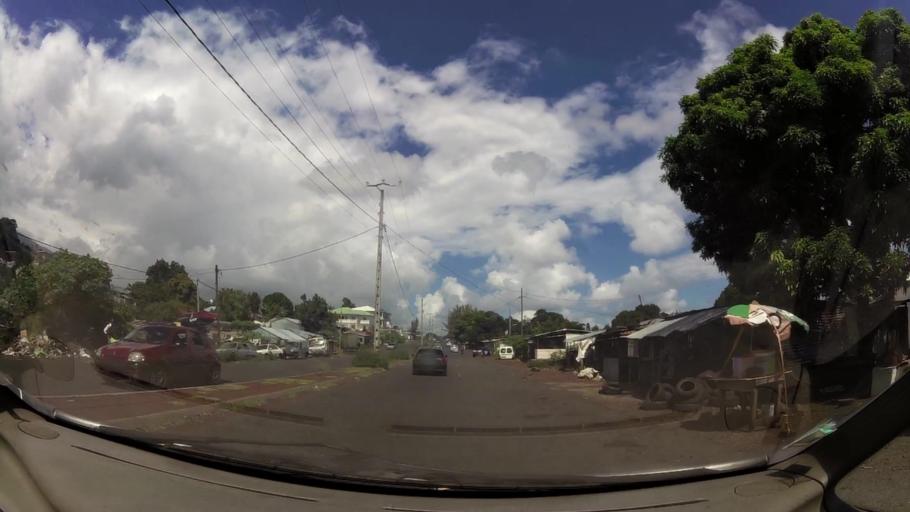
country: KM
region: Grande Comore
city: Mavingouni
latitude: -11.7212
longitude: 43.2451
